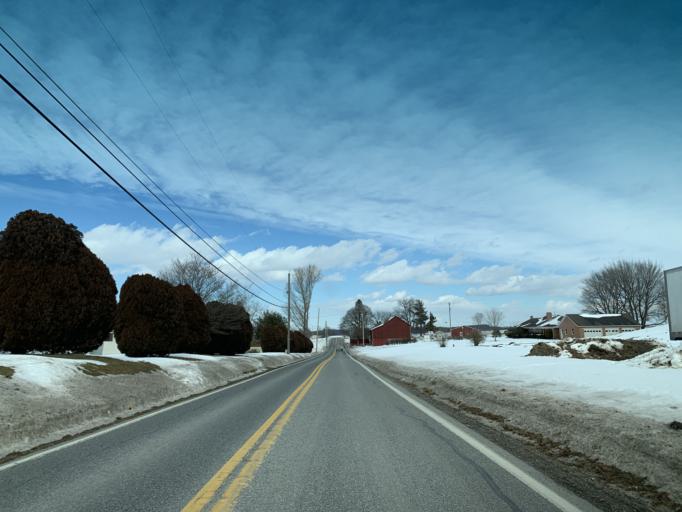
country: US
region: Pennsylvania
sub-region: York County
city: Shrewsbury
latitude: 39.7930
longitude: -76.6349
